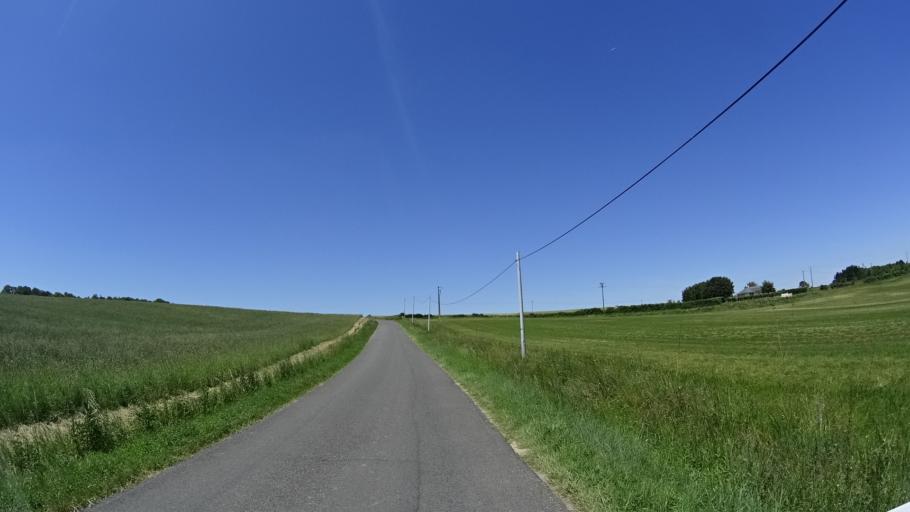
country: FR
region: Pays de la Loire
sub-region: Departement de Maine-et-Loire
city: Chenehutte-Treves-Cunault
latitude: 47.2834
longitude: -0.1381
